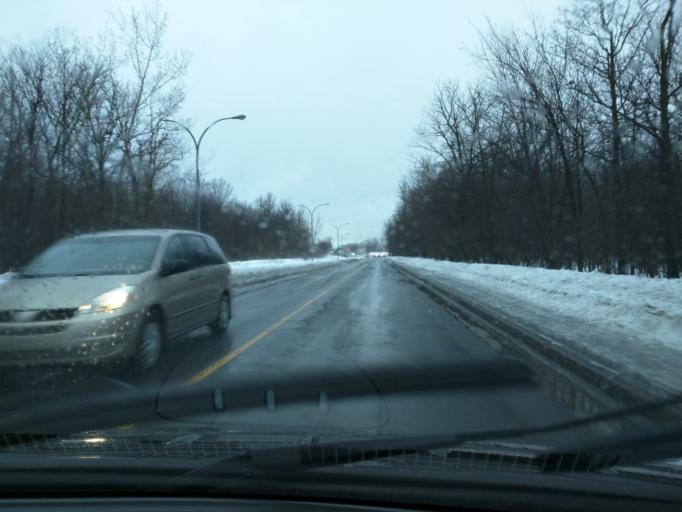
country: CA
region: Quebec
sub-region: Monteregie
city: Longueuil
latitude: 45.5481
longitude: -73.4889
